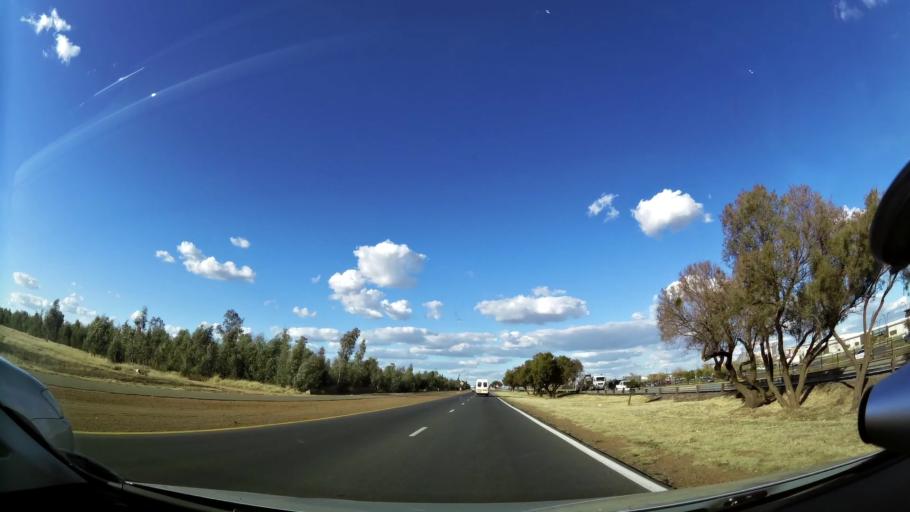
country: ZA
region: North-West
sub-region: Dr Kenneth Kaunda District Municipality
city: Klerksdorp
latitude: -26.8484
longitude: 26.7017
